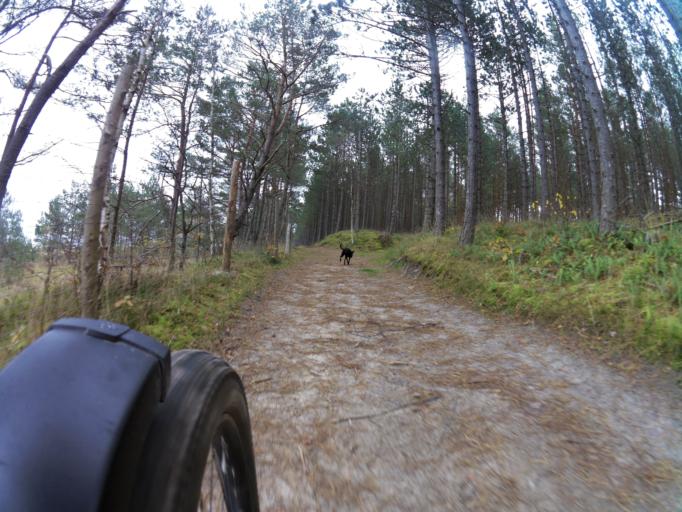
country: PL
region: Pomeranian Voivodeship
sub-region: Powiat pucki
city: Krokowa
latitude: 54.8320
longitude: 18.1001
